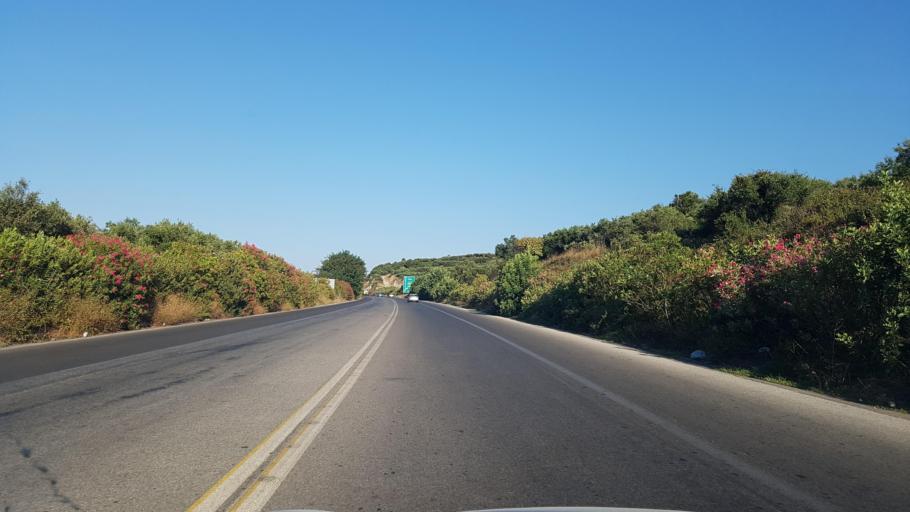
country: GR
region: Crete
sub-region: Nomos Chanias
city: Kolympari
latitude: 35.5249
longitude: 23.8032
